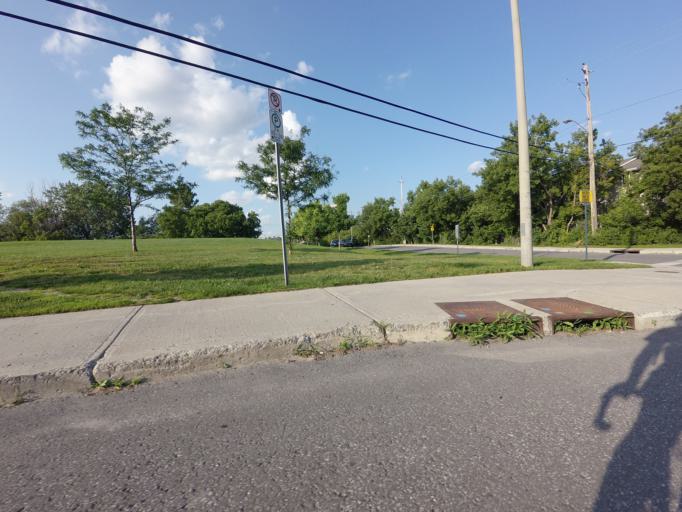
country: CA
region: Ontario
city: Ottawa
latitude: 45.4075
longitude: -75.7214
